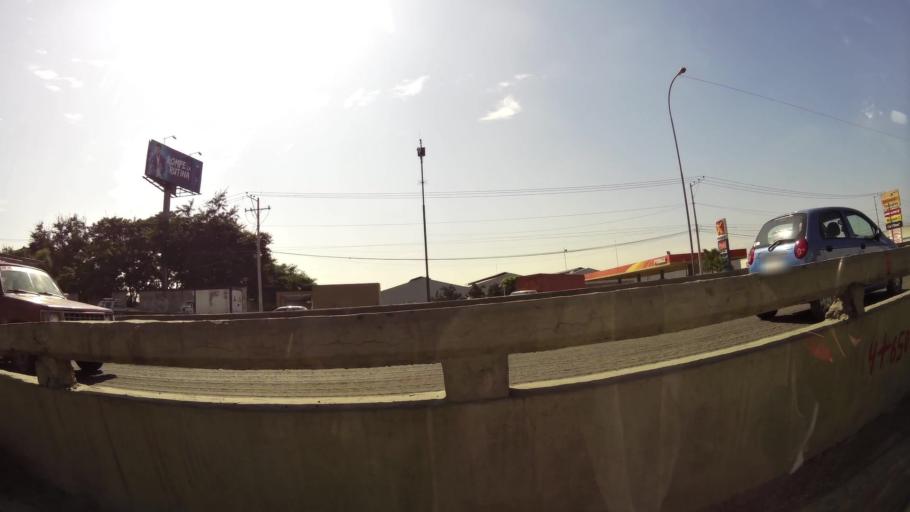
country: EC
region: Guayas
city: Guayaquil
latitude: -2.1211
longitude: -79.9316
